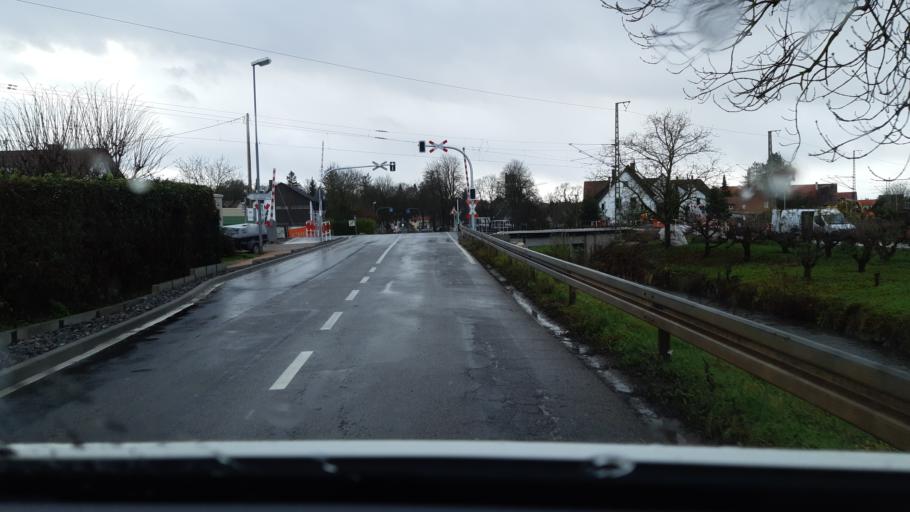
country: DE
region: Baden-Wuerttemberg
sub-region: Freiburg Region
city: Gottenheim
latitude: 48.0521
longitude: 7.7335
